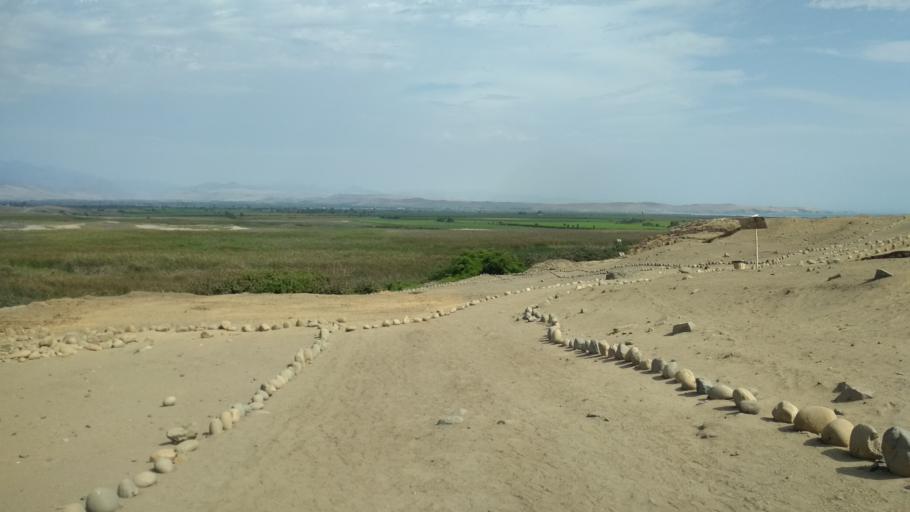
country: PE
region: Lima
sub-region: Barranca
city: Puerto Supe
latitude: -10.8150
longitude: -77.7412
